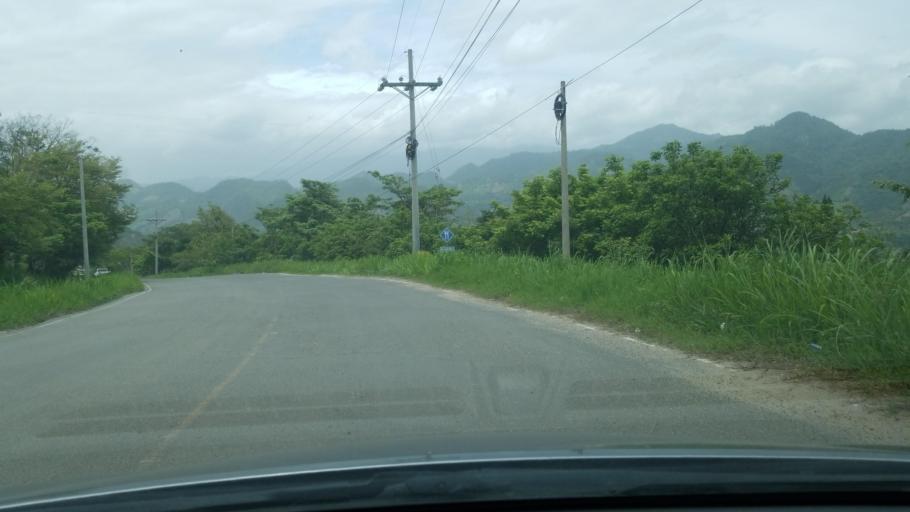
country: HN
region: Copan
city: Santa Rosa de Copan
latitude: 14.7327
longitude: -88.7735
